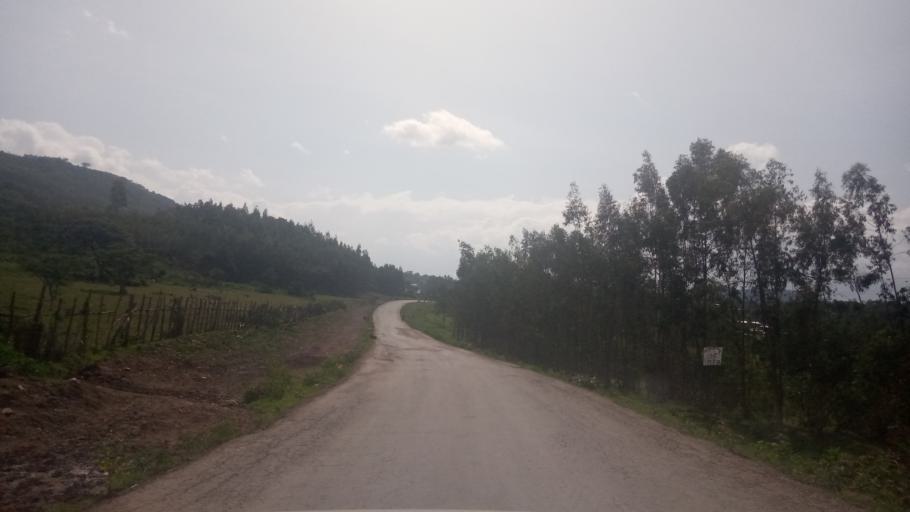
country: ET
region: Oromiya
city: Agaro
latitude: 7.9958
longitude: 36.5035
